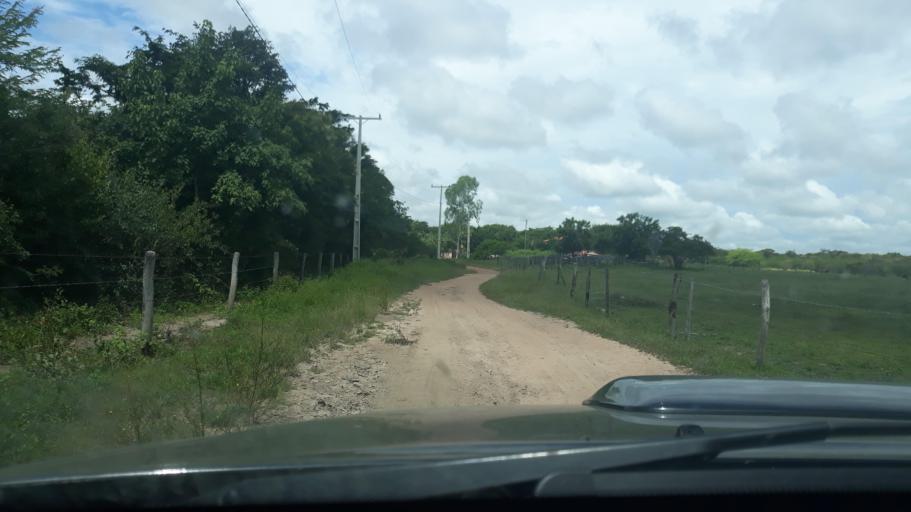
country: BR
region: Bahia
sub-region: Riacho De Santana
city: Riacho de Santana
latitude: -13.8627
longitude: -43.0736
